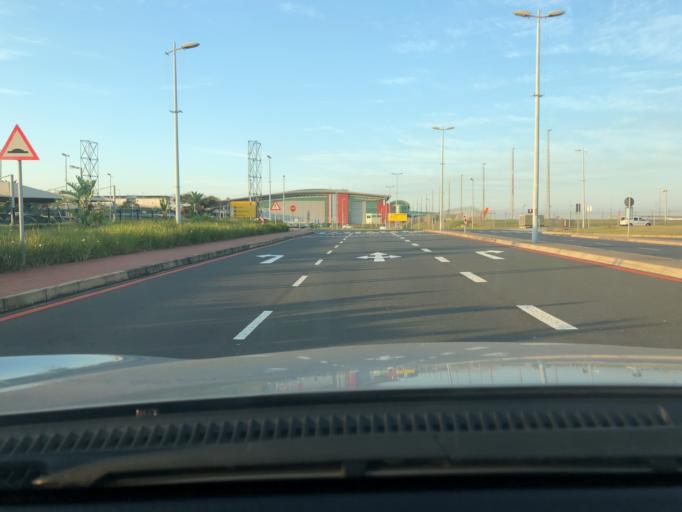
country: ZA
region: KwaZulu-Natal
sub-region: iLembe District Municipality
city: Ballitoville
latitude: -29.6230
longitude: 31.1019
